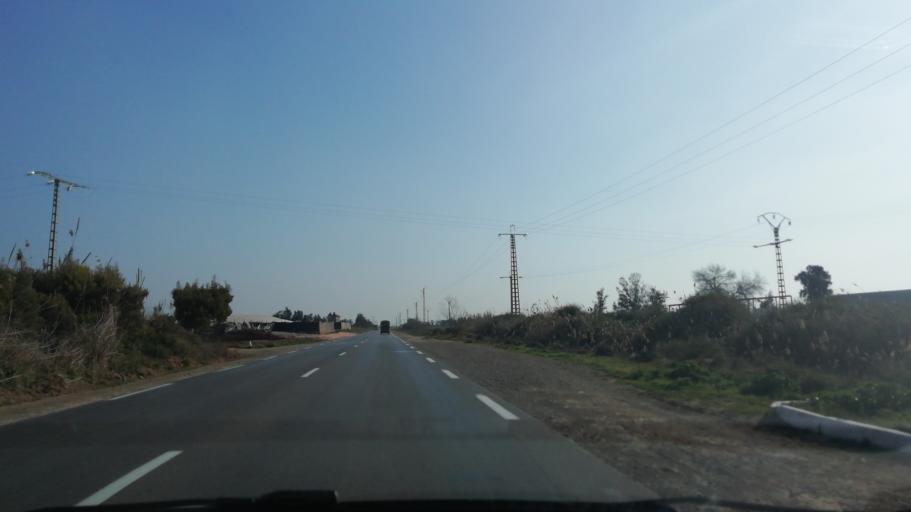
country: DZ
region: Mostaganem
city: Mostaganem
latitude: 35.7444
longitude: 0.0151
